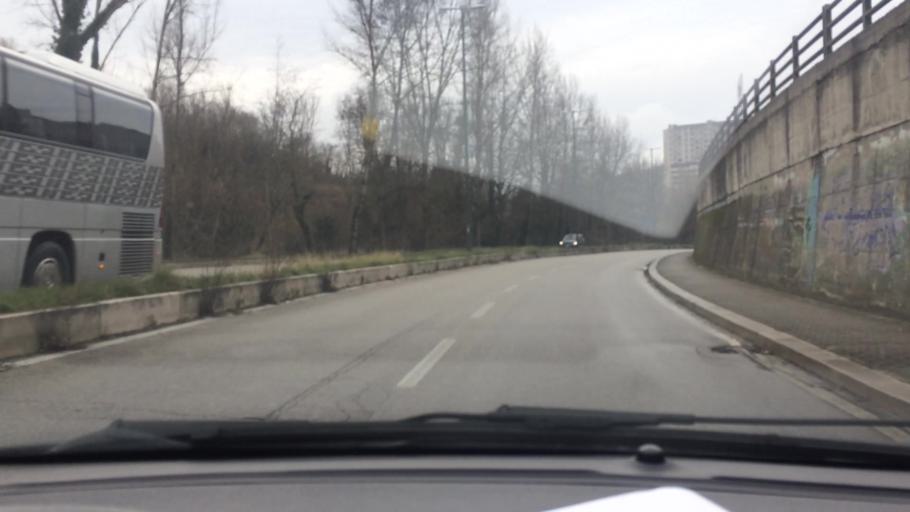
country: IT
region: Basilicate
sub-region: Provincia di Potenza
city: Potenza
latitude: 40.6351
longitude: 15.7953
